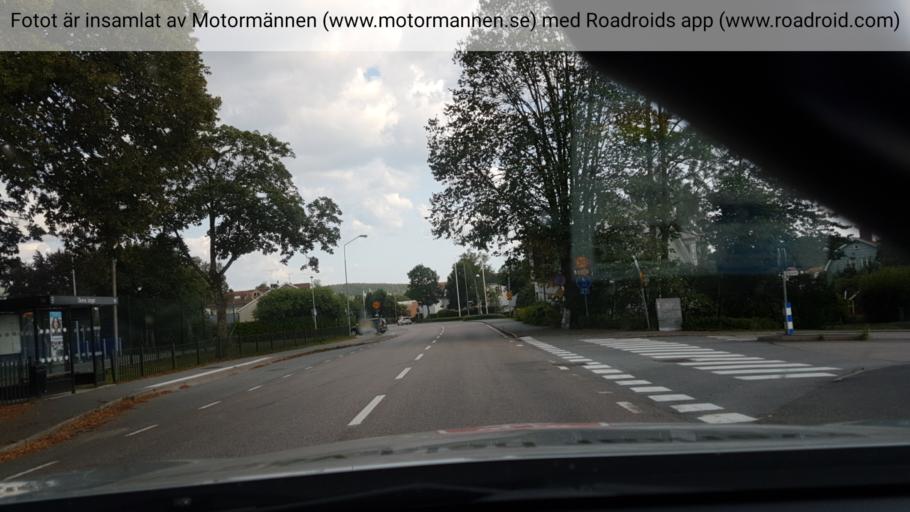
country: SE
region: Vaestra Goetaland
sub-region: Marks Kommun
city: Kinna
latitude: 57.4897
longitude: 12.6420
